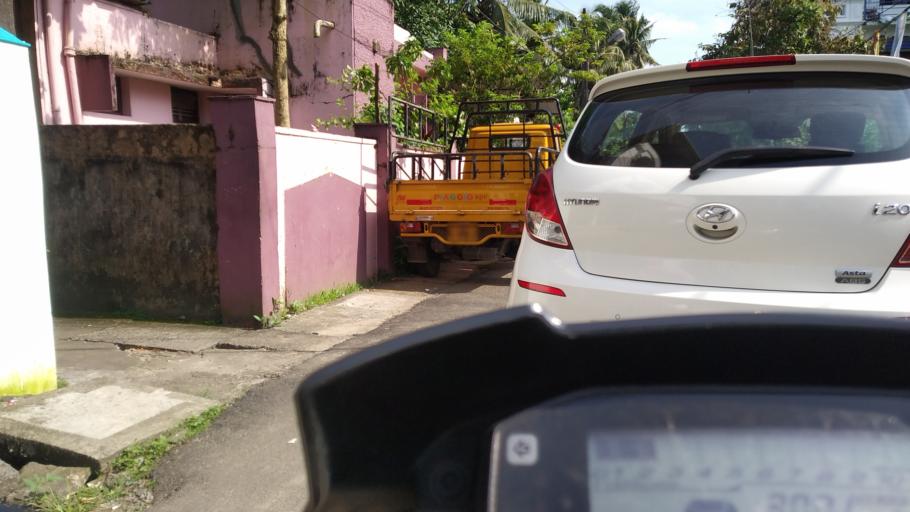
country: IN
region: Kerala
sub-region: Ernakulam
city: Cochin
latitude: 9.9814
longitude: 76.2937
